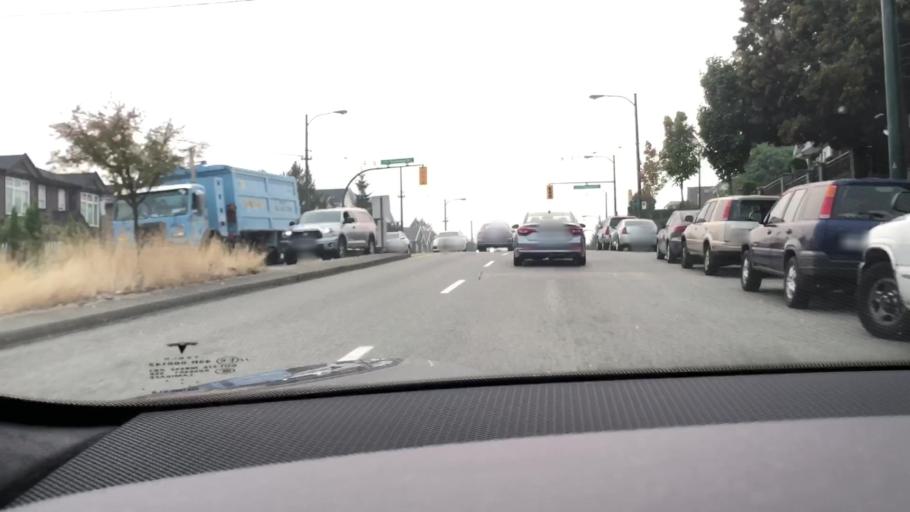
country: CA
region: British Columbia
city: Vancouver
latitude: 49.2328
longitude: -123.0788
